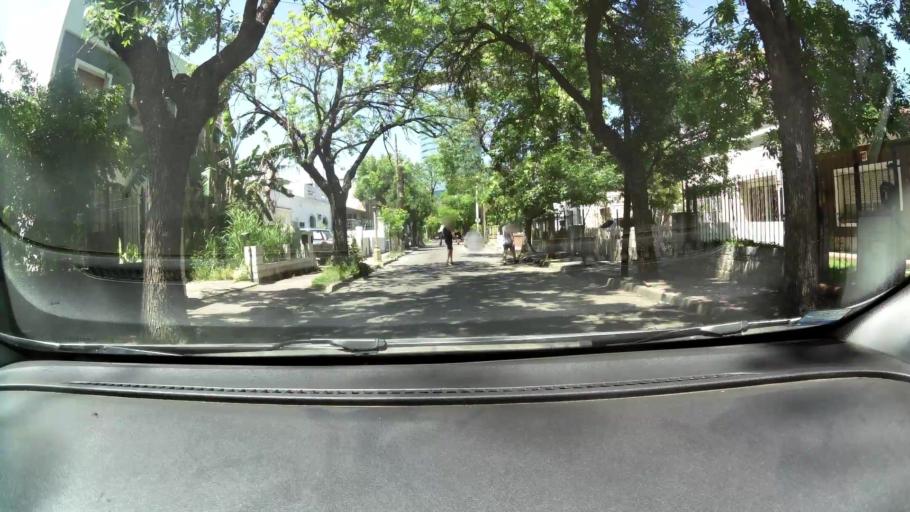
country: AR
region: Cordoba
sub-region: Departamento de Capital
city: Cordoba
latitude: -31.4114
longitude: -64.2019
